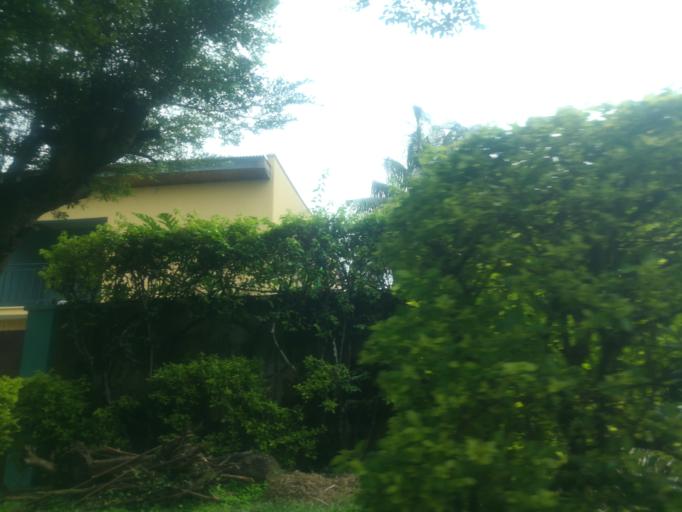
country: NG
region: Oyo
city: Ibadan
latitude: 7.4245
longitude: 3.9131
